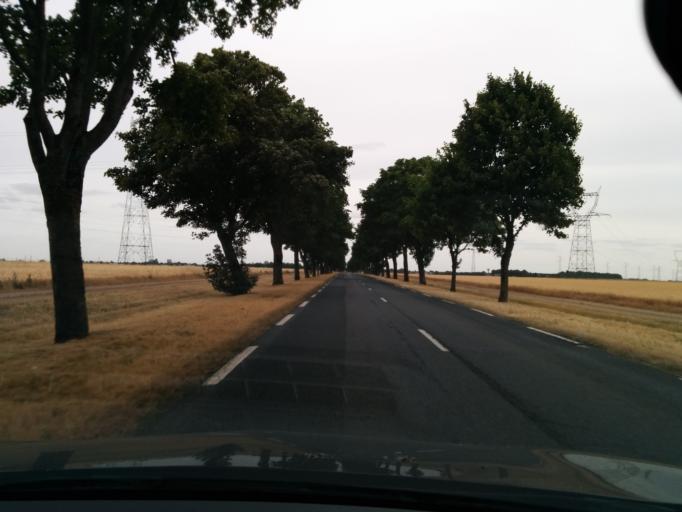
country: FR
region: Ile-de-France
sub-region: Departement de l'Essonne
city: Pussay
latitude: 48.3347
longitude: 1.9914
